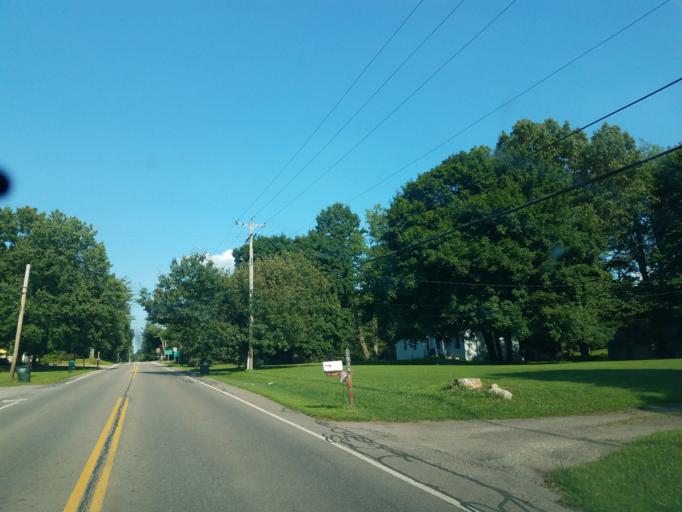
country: US
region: Ohio
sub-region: Stark County
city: Uniontown
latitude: 40.9763
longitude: -81.4182
